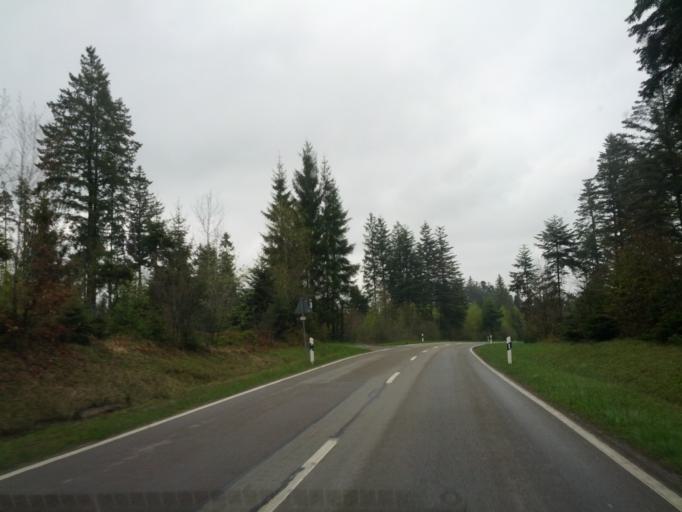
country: DE
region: Baden-Wuerttemberg
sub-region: Freiburg Region
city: Rickenbach
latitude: 47.6087
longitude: 8.0154
